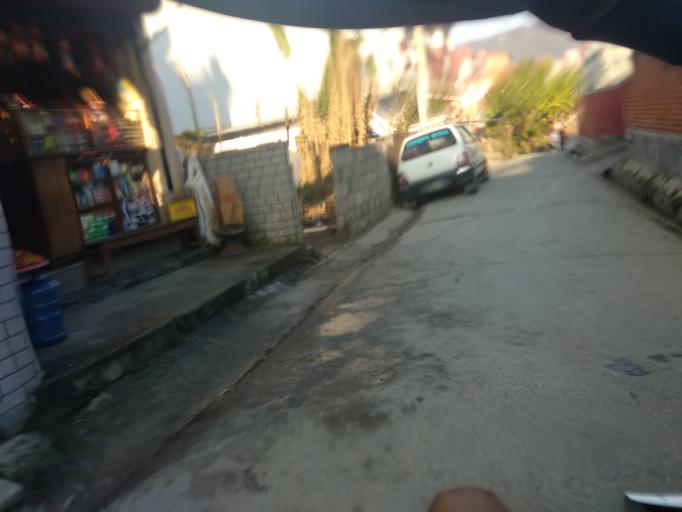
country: NP
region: Western Region
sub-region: Gandaki Zone
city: Pokhara
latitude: 28.2140
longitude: 83.9795
